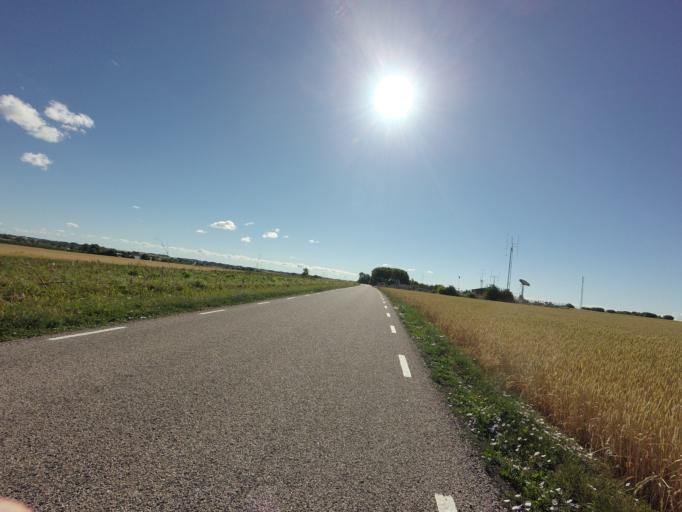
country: SE
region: Skane
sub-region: Trelleborgs Kommun
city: Skare
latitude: 55.3904
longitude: 13.0653
